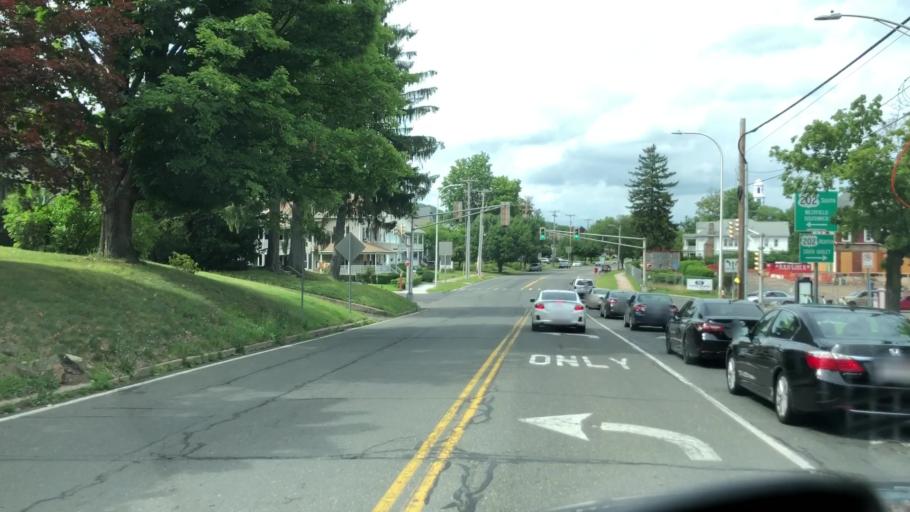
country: US
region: Massachusetts
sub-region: Hampden County
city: Holyoke
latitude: 42.1984
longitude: -72.6311
